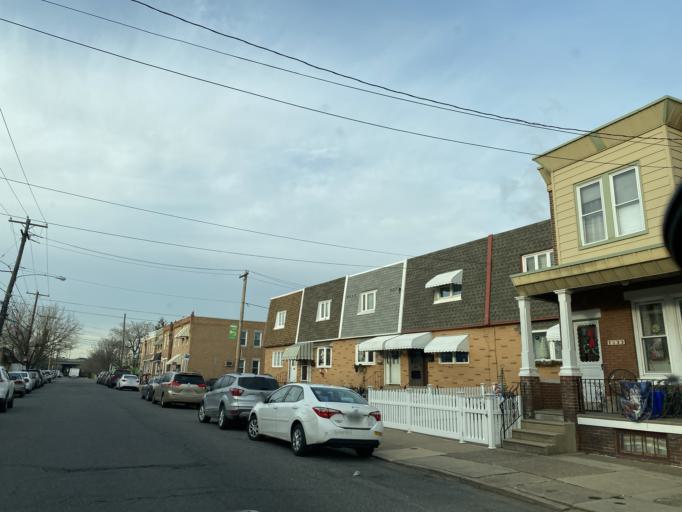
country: US
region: New Jersey
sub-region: Burlington County
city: Palmyra
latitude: 40.0023
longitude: -75.0738
